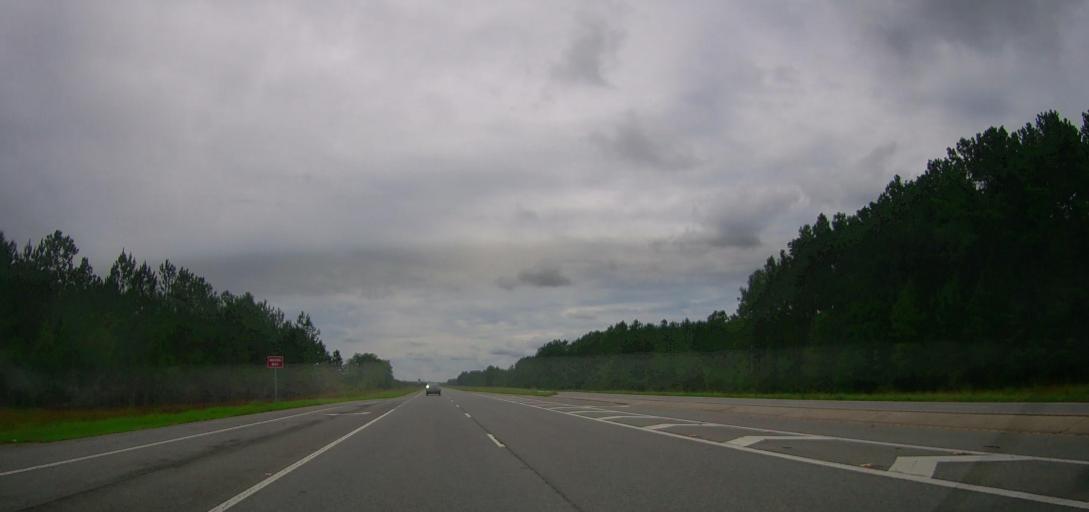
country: US
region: Georgia
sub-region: Appling County
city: Baxley
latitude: 31.7444
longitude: -82.2505
